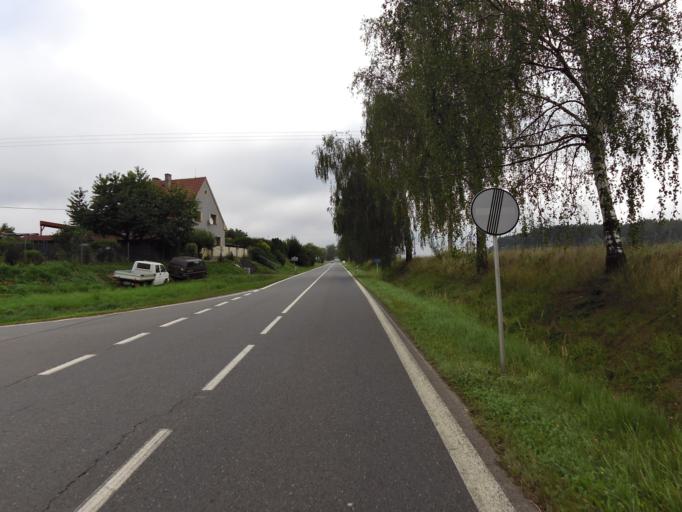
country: CZ
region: Jihocesky
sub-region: Okres Tabor
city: Sezimovo Usti
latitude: 49.4294
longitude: 14.7190
